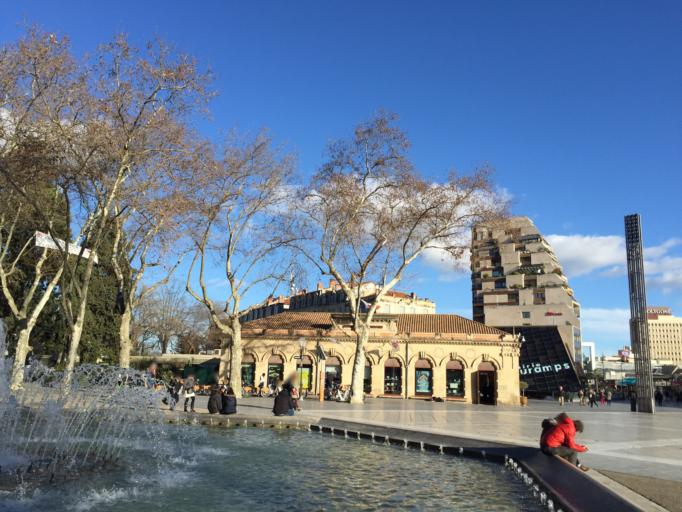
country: FR
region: Languedoc-Roussillon
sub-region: Departement de l'Herault
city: Montpellier
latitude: 43.6096
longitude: 3.8807
